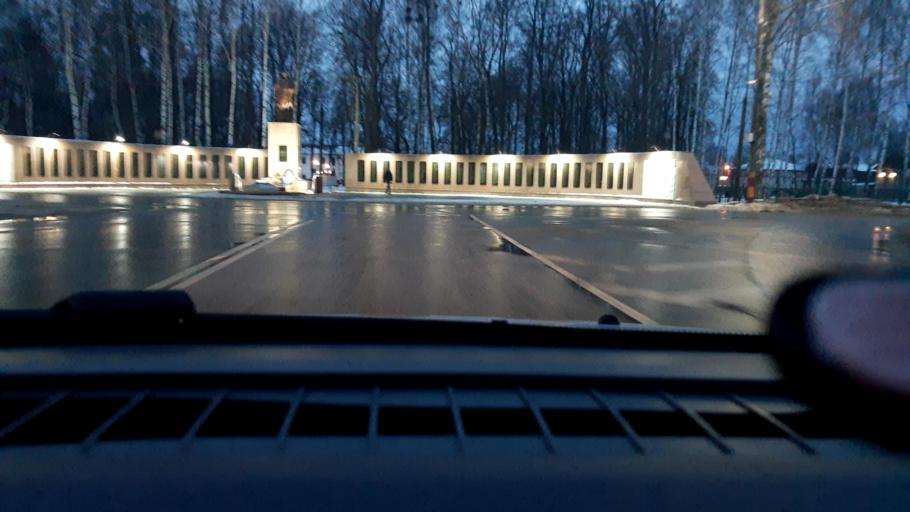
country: RU
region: Nizjnij Novgorod
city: Lyskovo
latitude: 56.0389
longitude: 45.0459
